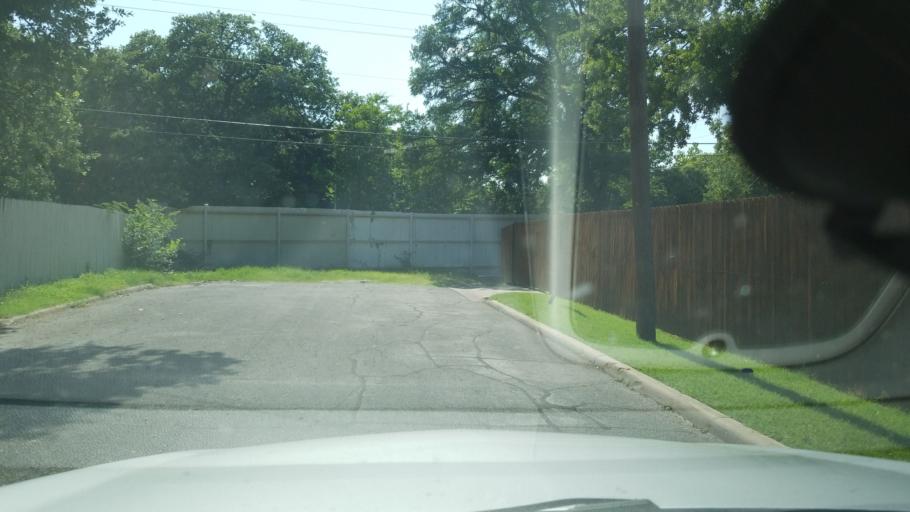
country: US
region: Texas
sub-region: Dallas County
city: Irving
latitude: 32.8125
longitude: -96.9702
